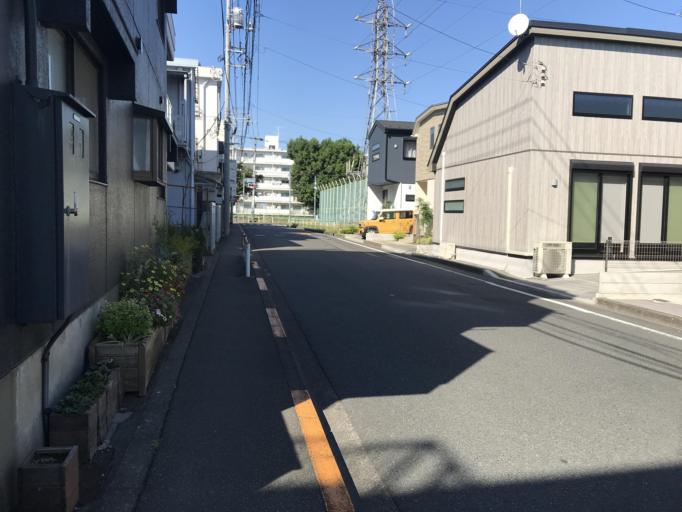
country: JP
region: Tokyo
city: Higashimurayama-shi
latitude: 35.7335
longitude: 139.4713
